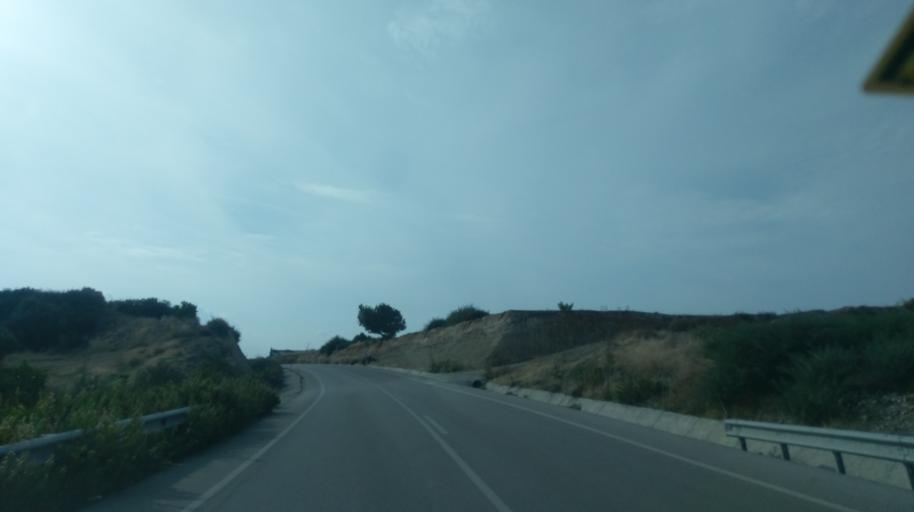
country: CY
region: Ammochostos
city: Trikomo
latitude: 35.4293
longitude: 33.9190
